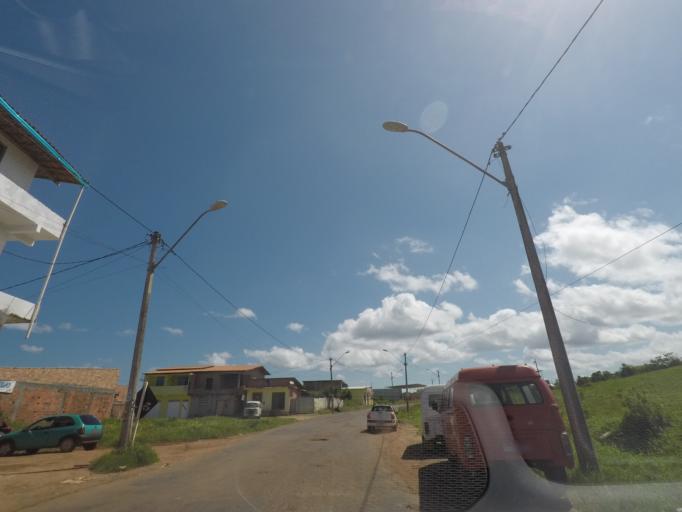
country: BR
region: Bahia
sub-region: Taperoa
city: Taperoa
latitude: -13.5482
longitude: -39.0989
